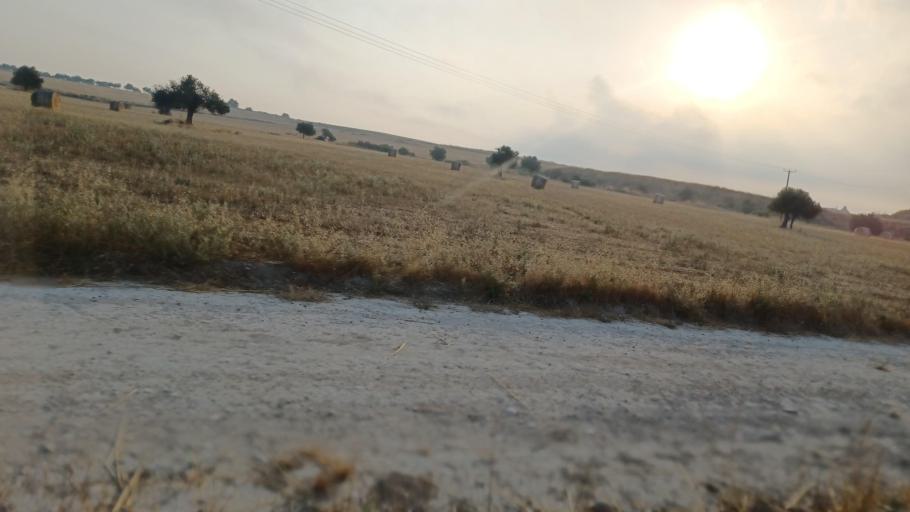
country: CY
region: Larnaka
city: Tersefanou
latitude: 34.8332
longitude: 33.5222
